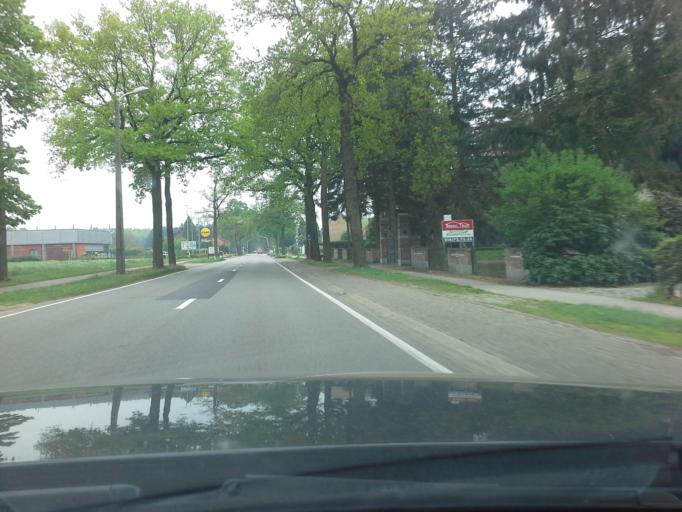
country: BE
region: Flanders
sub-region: Provincie Antwerpen
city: Kasterlee
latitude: 51.2287
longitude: 4.9729
